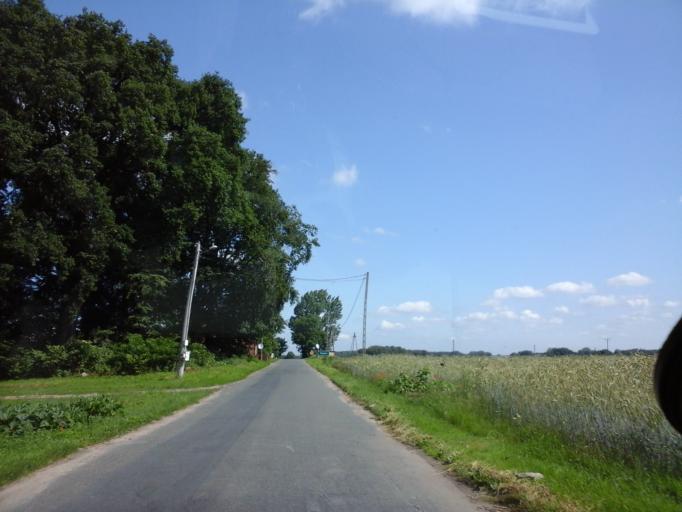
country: PL
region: West Pomeranian Voivodeship
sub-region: Powiat choszczenski
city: Recz
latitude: 53.2233
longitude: 15.5489
